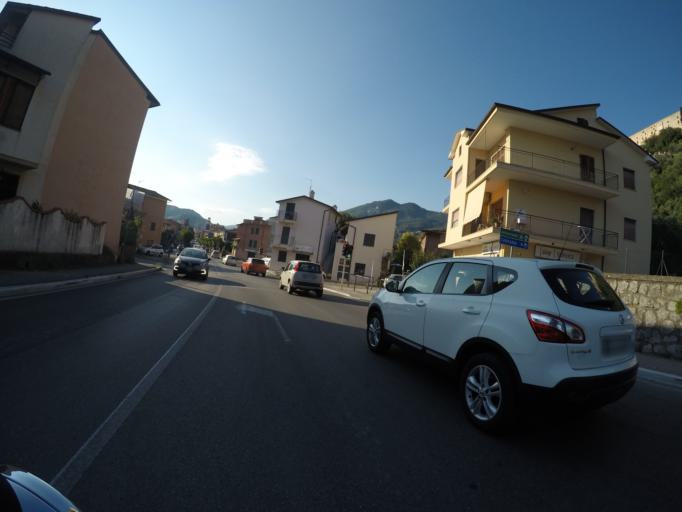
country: IT
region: Tuscany
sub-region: Provincia di Massa-Carrara
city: Massa
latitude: 44.0313
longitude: 10.1442
